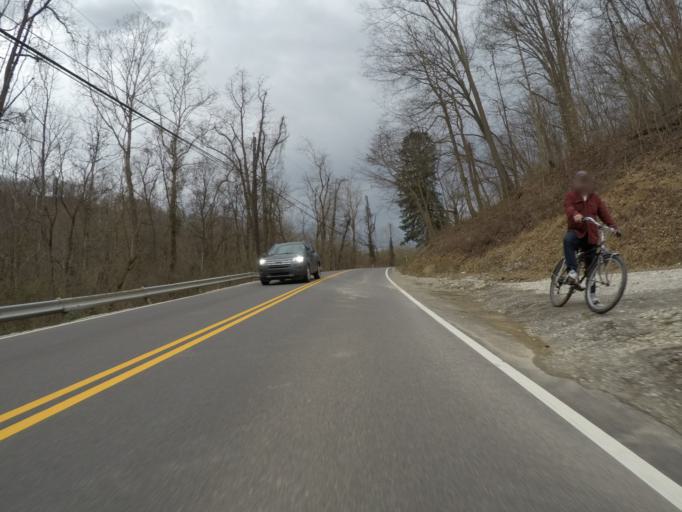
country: US
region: West Virginia
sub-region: Cabell County
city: Huntington
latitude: 38.4293
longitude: -82.4915
